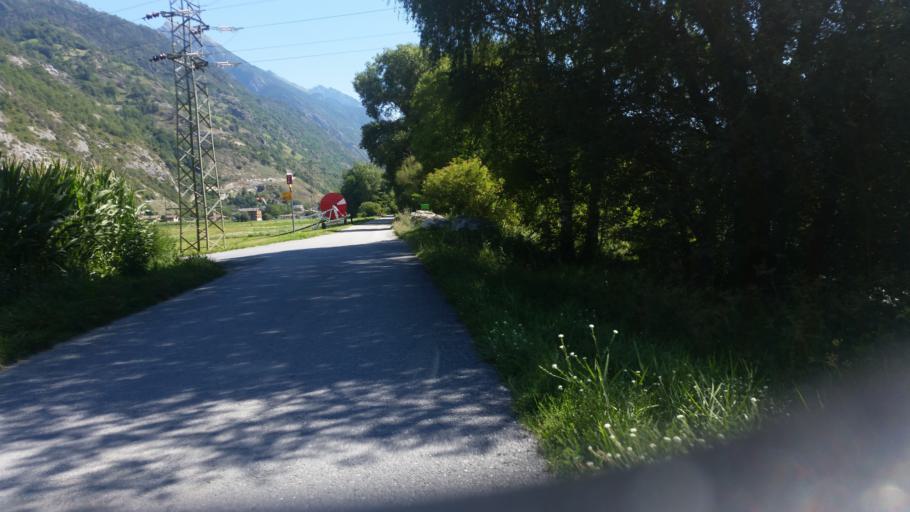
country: CH
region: Valais
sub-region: Leuk District
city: Turtmann
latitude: 46.3083
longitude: 7.6884
